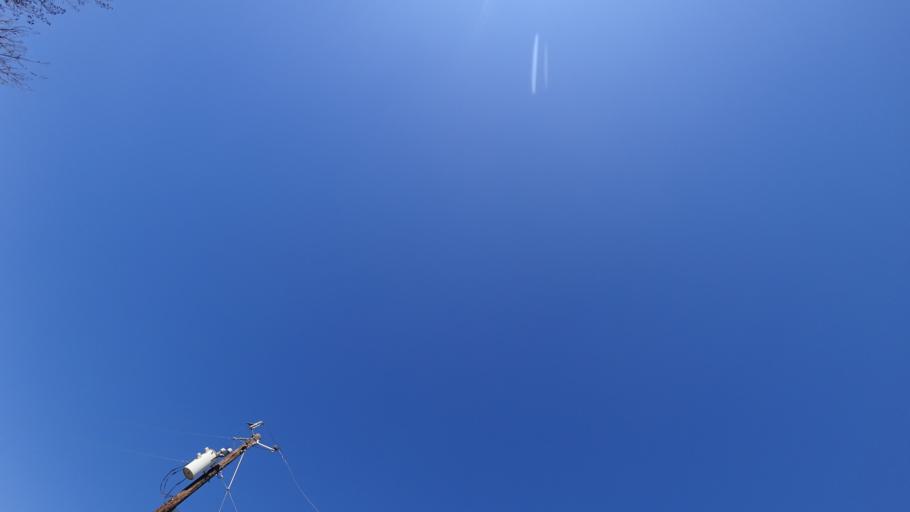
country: US
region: Texas
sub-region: Denton County
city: Lewisville
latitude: 33.0343
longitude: -96.9370
